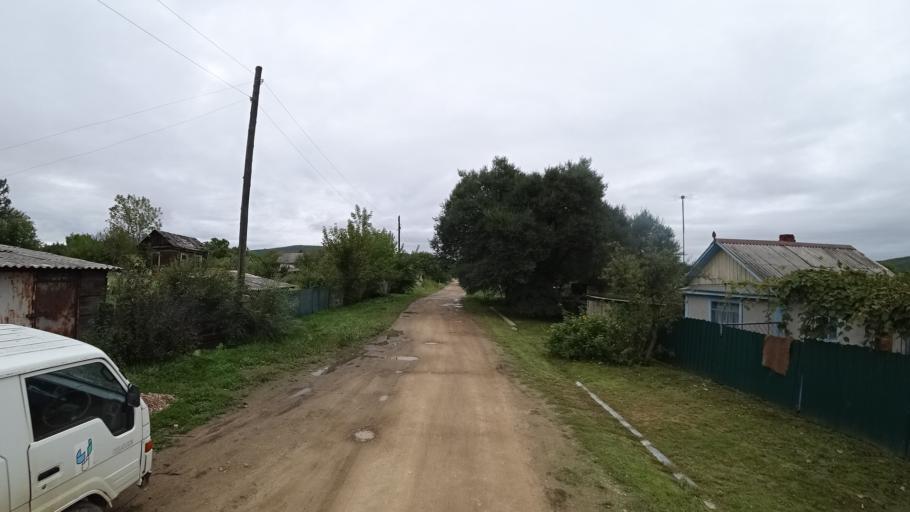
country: RU
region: Primorskiy
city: Rettikhovka
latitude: 44.1698
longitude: 132.7669
